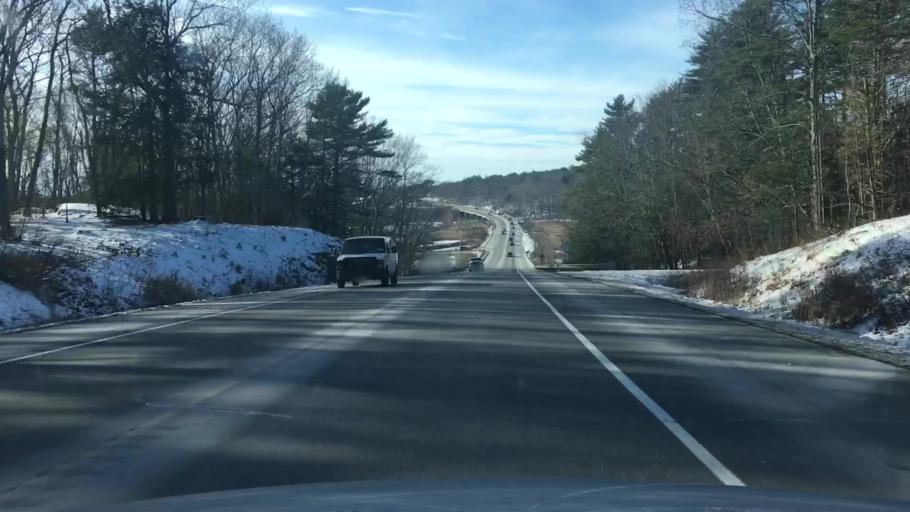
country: US
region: Maine
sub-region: Sagadahoc County
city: Woolwich
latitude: 43.9266
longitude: -69.7904
